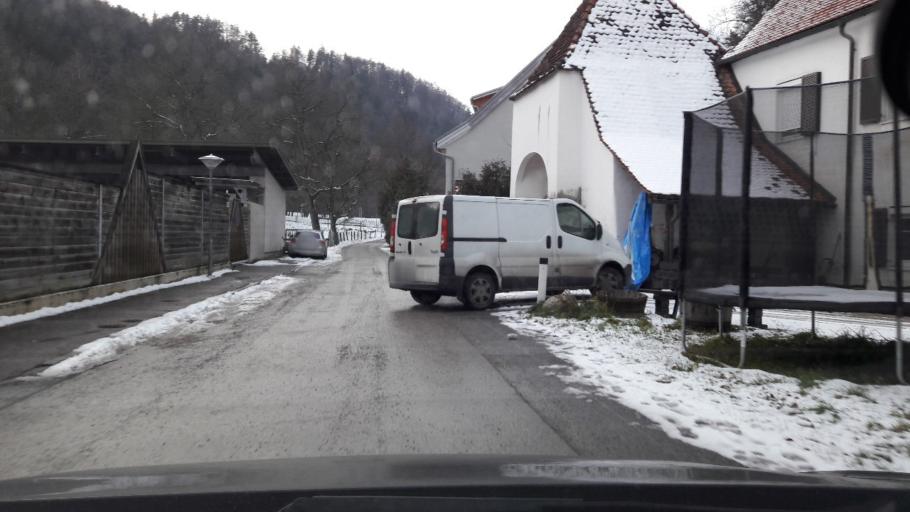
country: AT
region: Styria
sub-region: Politischer Bezirk Graz-Umgebung
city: Eisbach
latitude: 47.1371
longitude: 15.2851
